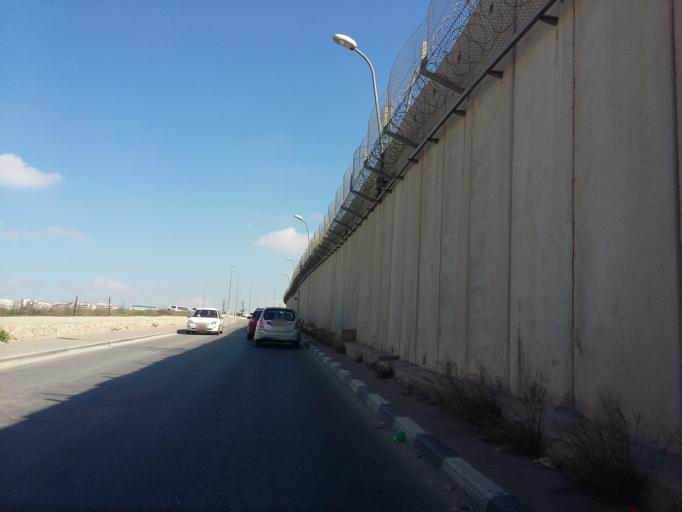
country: PS
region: West Bank
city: Ar Ram wa Dahiyat al Barid
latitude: 31.8581
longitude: 35.2252
